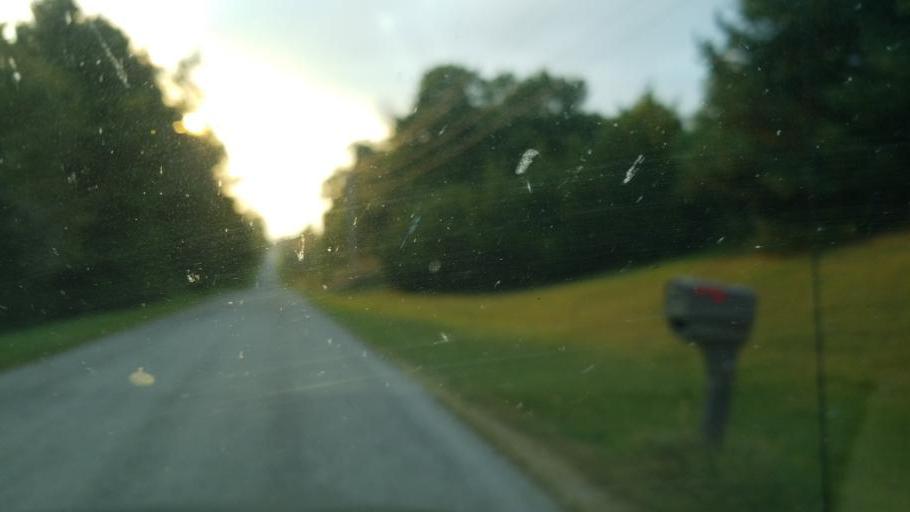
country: US
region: Ohio
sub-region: Morrow County
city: Mount Gilead
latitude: 40.5216
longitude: -82.7200
